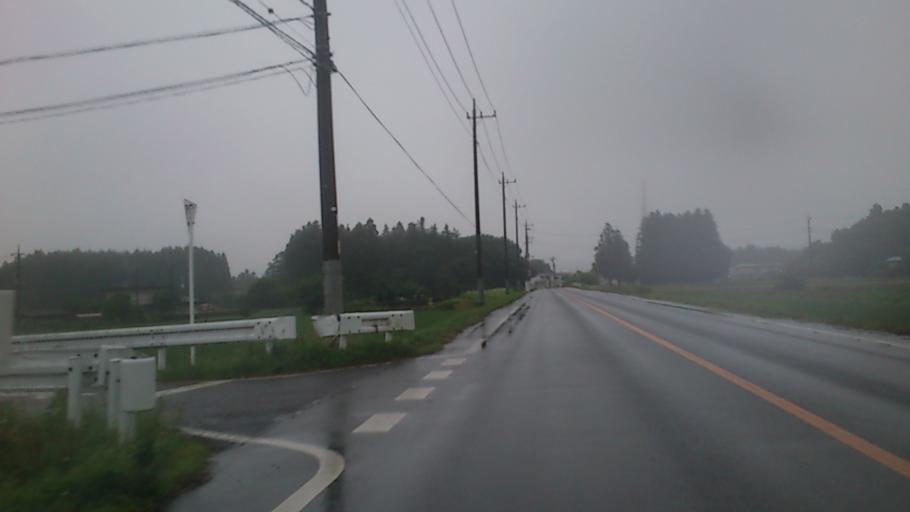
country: JP
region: Tochigi
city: Otawara
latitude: 36.9049
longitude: 139.9950
